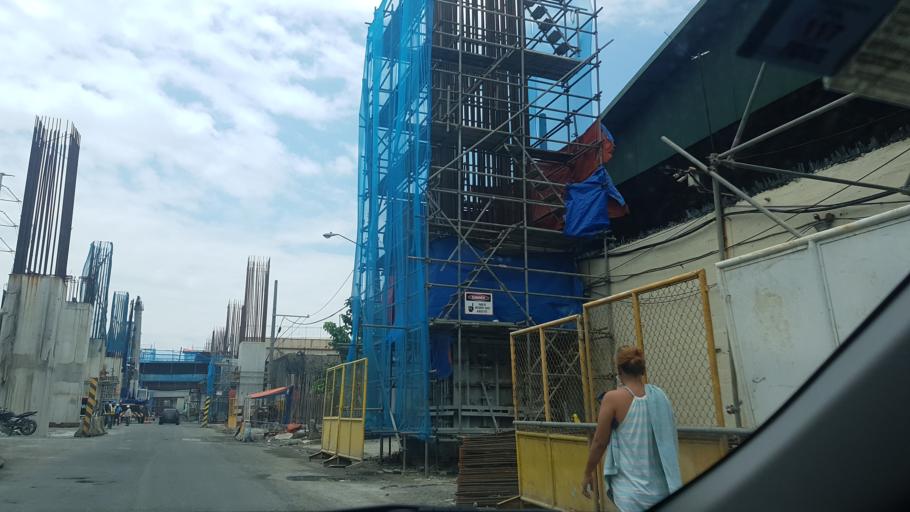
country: PH
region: Calabarzon
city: Del Monte
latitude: 14.6420
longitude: 121.0060
